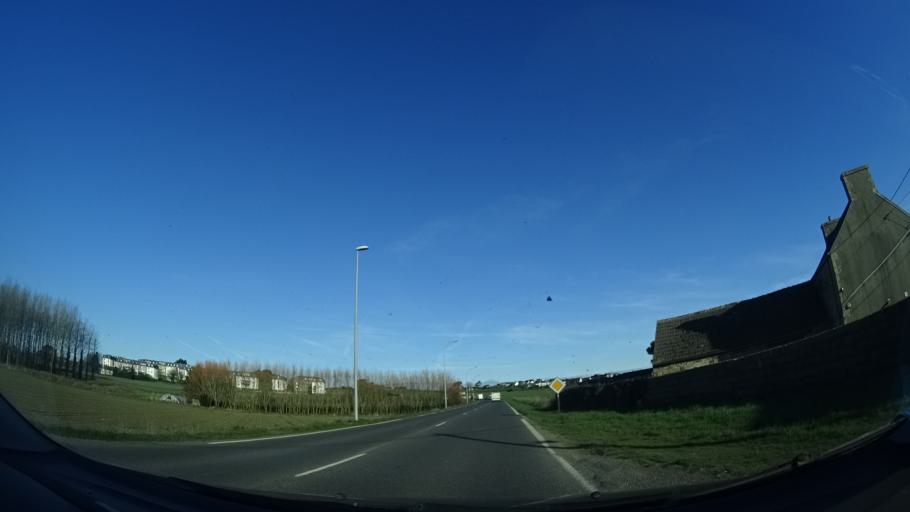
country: FR
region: Brittany
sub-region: Departement du Finistere
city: Saint-Pol-de-Leon
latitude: 48.6821
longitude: -4.0024
